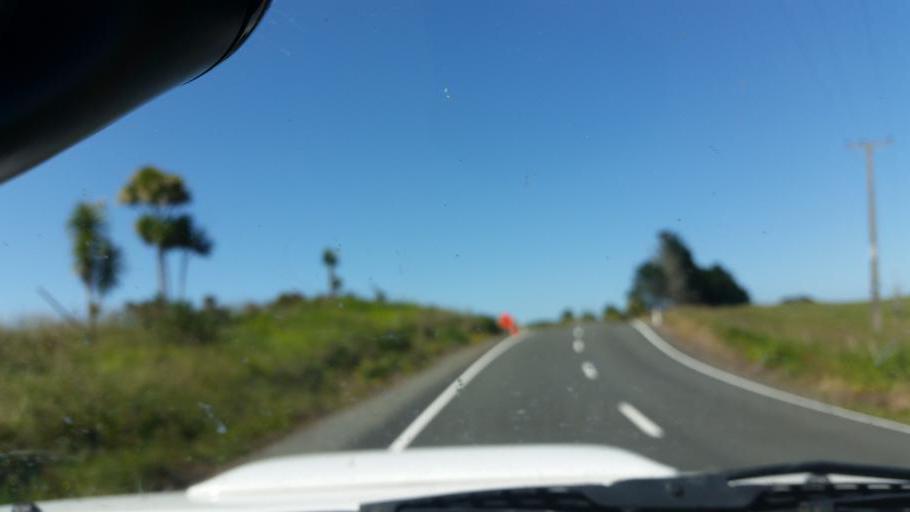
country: NZ
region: Auckland
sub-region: Auckland
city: Wellsford
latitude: -36.2215
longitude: 174.3798
